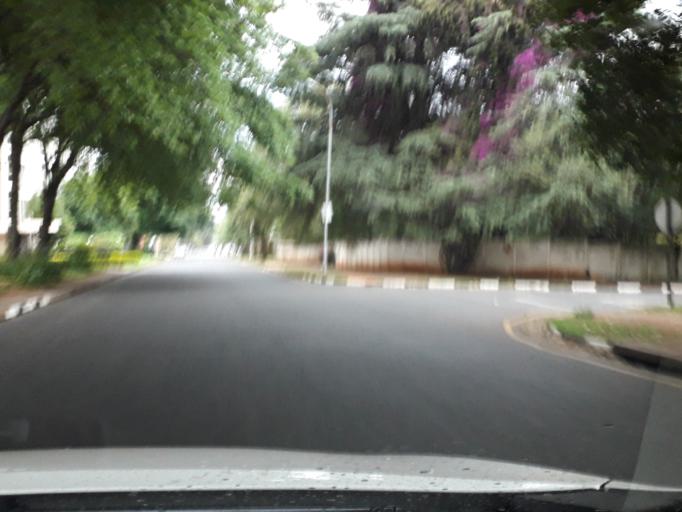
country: ZA
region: Gauteng
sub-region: City of Johannesburg Metropolitan Municipality
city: Johannesburg
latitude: -26.1373
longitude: 28.0555
